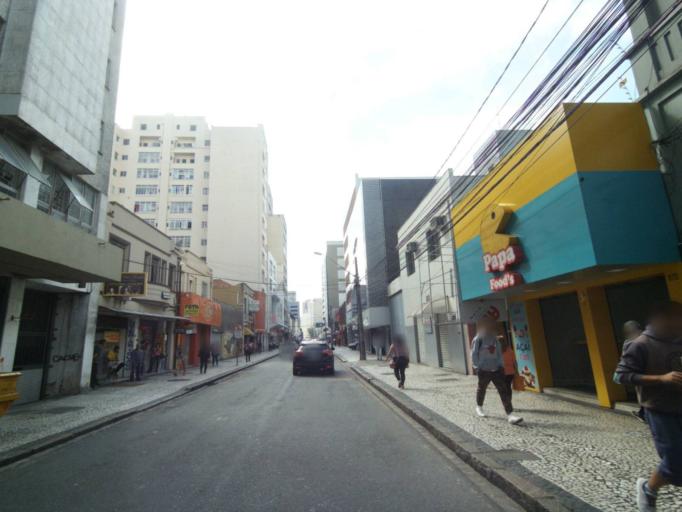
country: BR
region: Parana
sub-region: Curitiba
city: Curitiba
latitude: -25.4327
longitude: -49.2699
